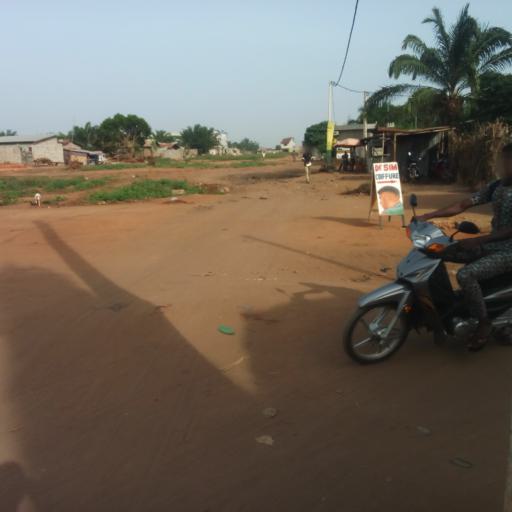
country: BJ
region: Atlantique
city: Abomey-Calavi
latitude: 6.4239
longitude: 2.3370
